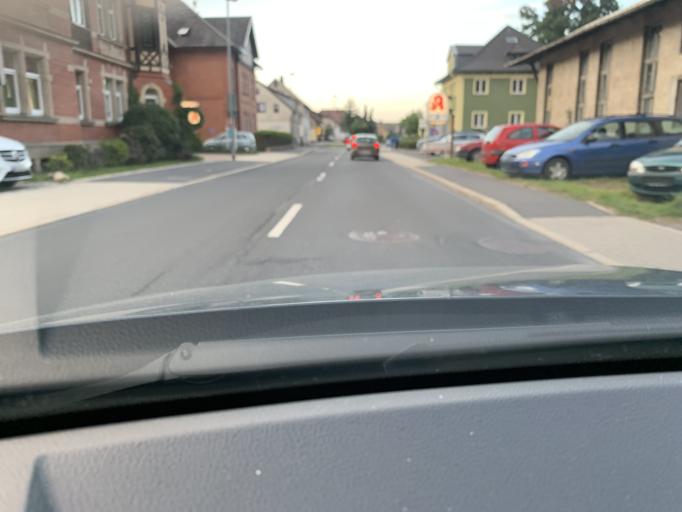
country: DE
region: Bavaria
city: Foritz
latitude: 50.3609
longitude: 11.2096
